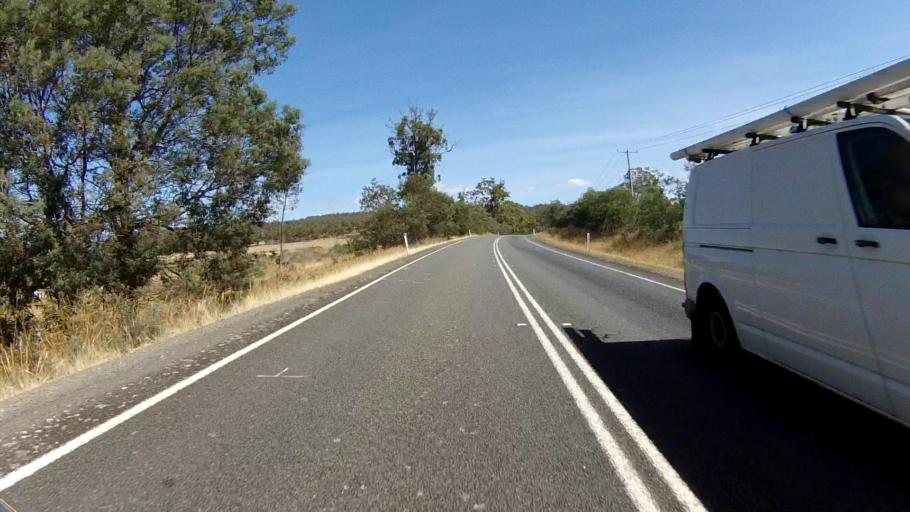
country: AU
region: Tasmania
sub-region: Sorell
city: Sorell
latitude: -42.5781
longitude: 147.8171
